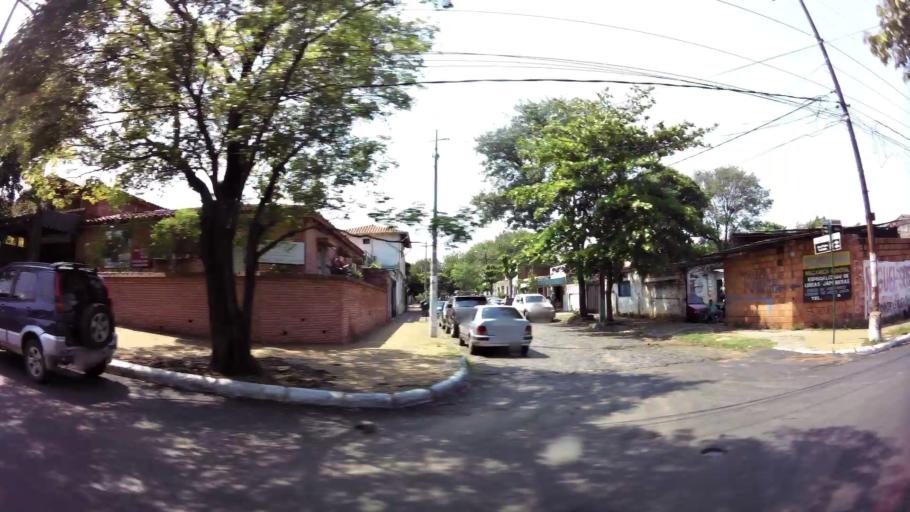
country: PY
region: Asuncion
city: Asuncion
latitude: -25.2917
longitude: -57.6507
